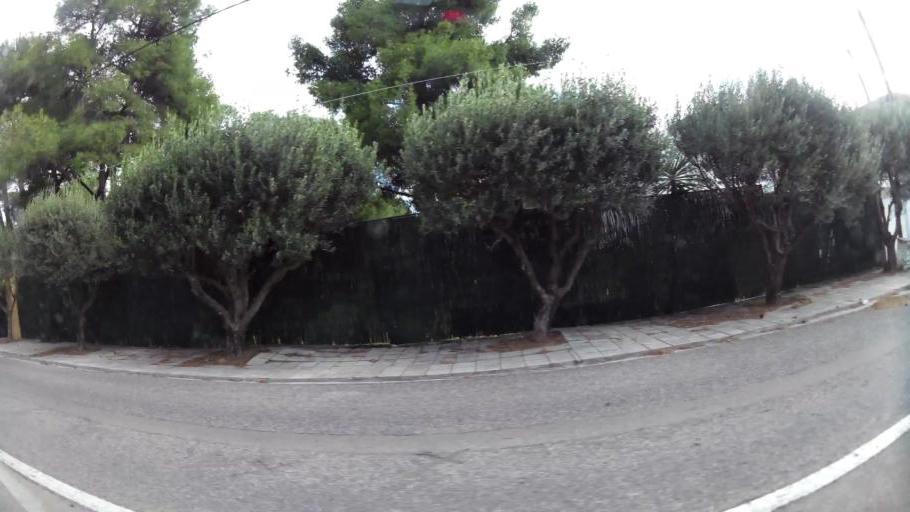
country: GR
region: Attica
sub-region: Nomarchia Anatolikis Attikis
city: Thrakomakedones
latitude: 38.1223
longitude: 23.7526
